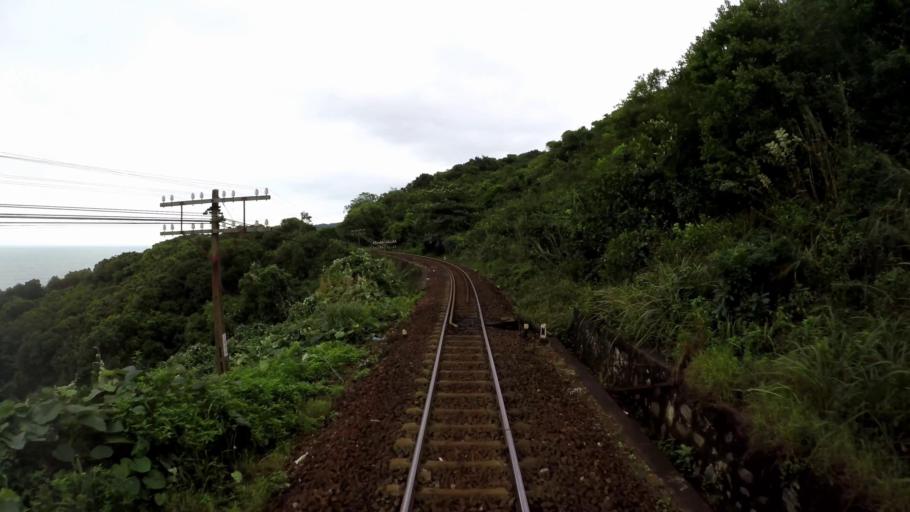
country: VN
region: Da Nang
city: Lien Chieu
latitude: 16.2146
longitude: 108.1267
